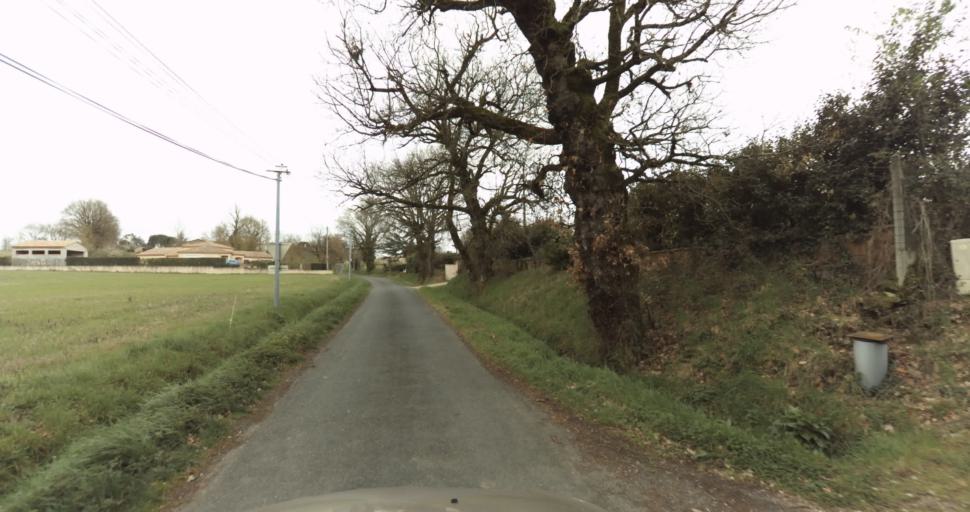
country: FR
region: Midi-Pyrenees
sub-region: Departement du Tarn
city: Puygouzon
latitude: 43.8899
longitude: 2.1595
